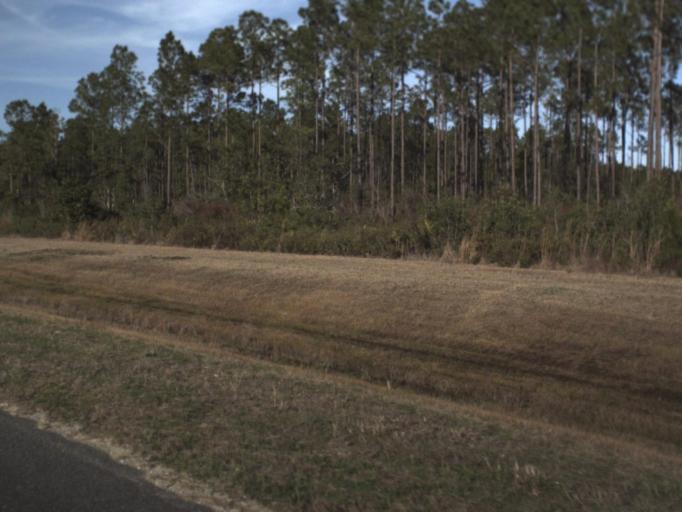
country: US
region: Florida
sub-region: Bay County
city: Laguna Beach
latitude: 30.3519
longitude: -85.8588
